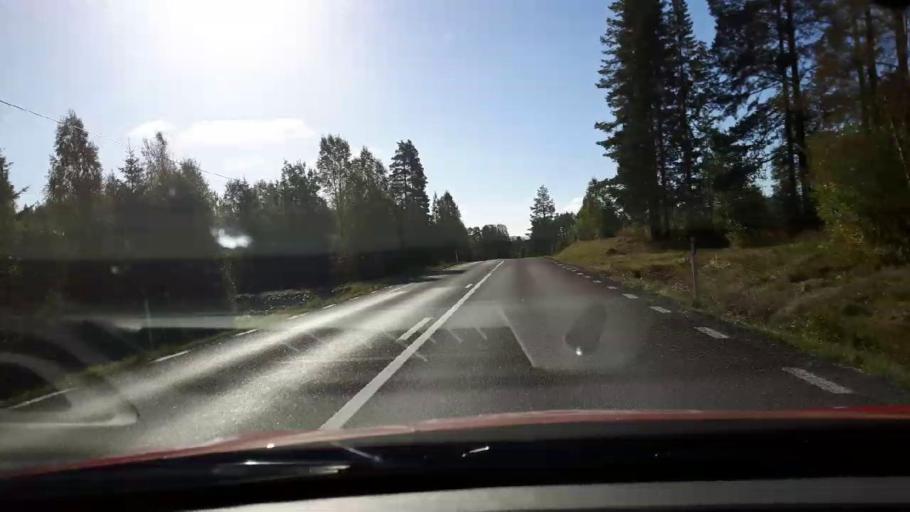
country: SE
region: Jaemtland
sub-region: OEstersunds Kommun
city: Brunflo
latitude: 62.9621
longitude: 15.0289
